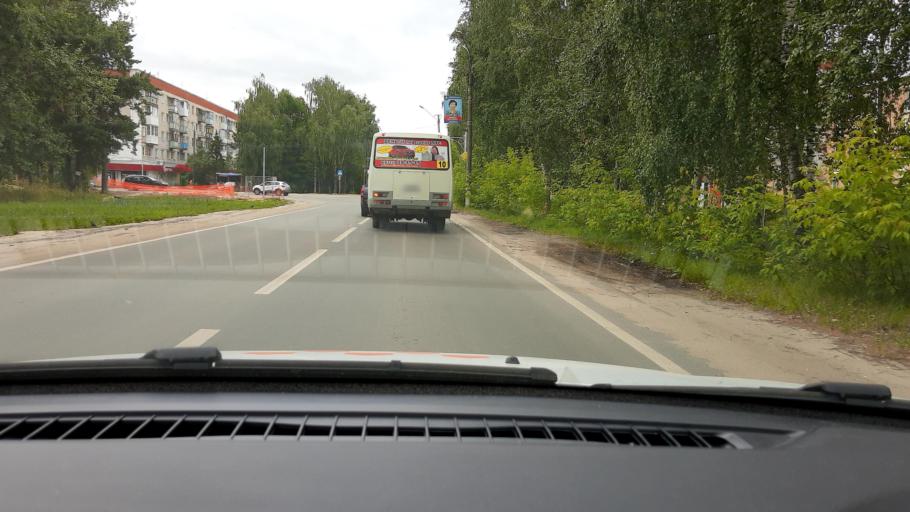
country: RU
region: Nizjnij Novgorod
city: Pyra
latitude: 56.2478
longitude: 43.3907
